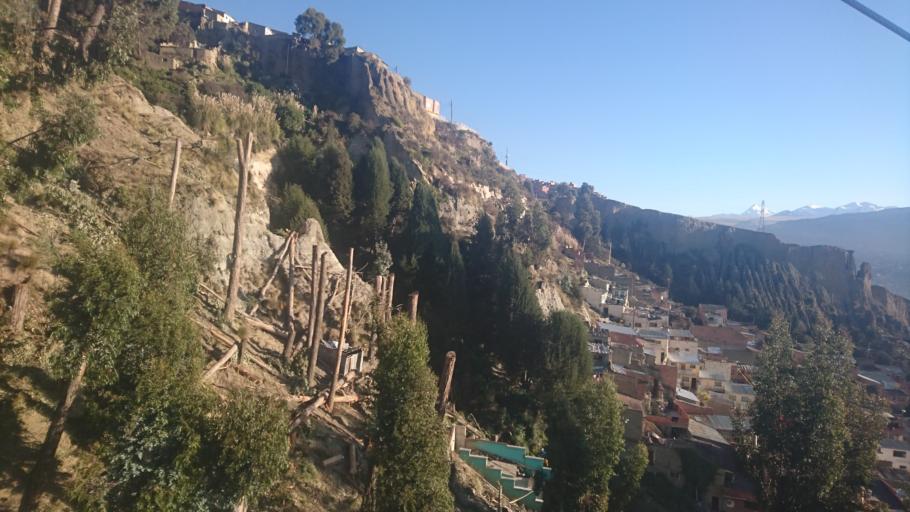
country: BO
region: La Paz
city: La Paz
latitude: -16.5158
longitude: -68.1451
